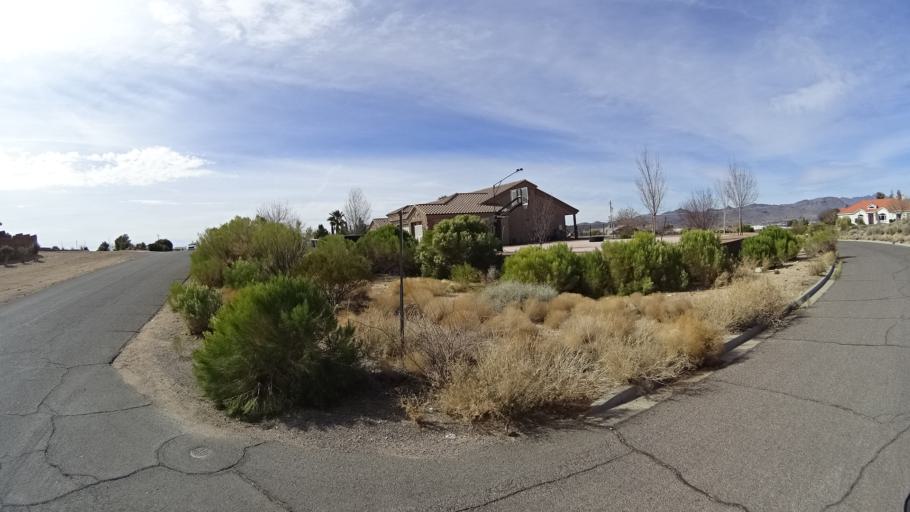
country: US
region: Arizona
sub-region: Mohave County
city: Kingman
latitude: 35.1867
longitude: -113.9896
